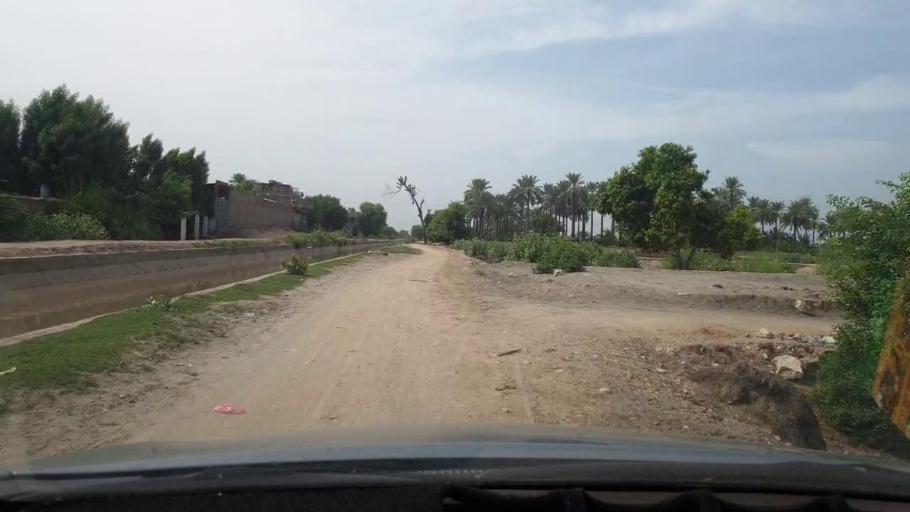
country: PK
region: Sindh
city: Khairpur
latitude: 27.5076
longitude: 68.7595
